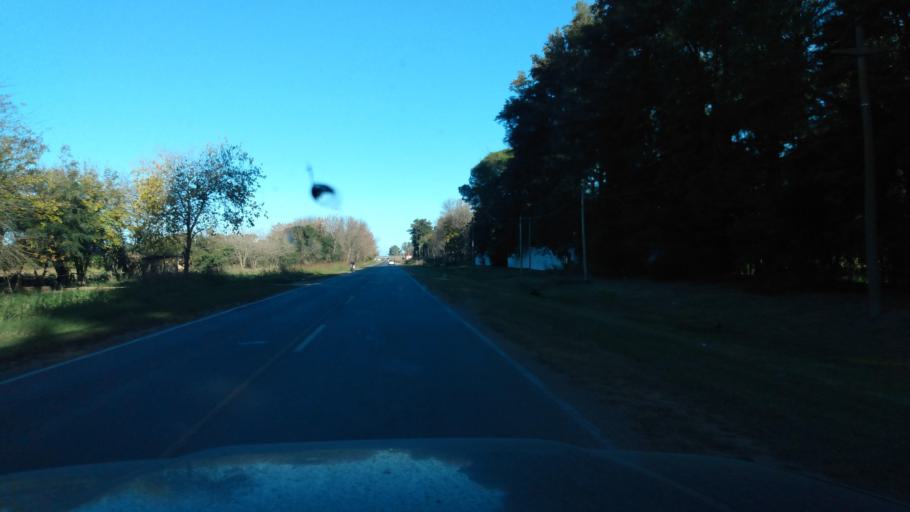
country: AR
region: Buenos Aires
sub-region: Partido de Lujan
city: Lujan
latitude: -34.5372
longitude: -59.1628
